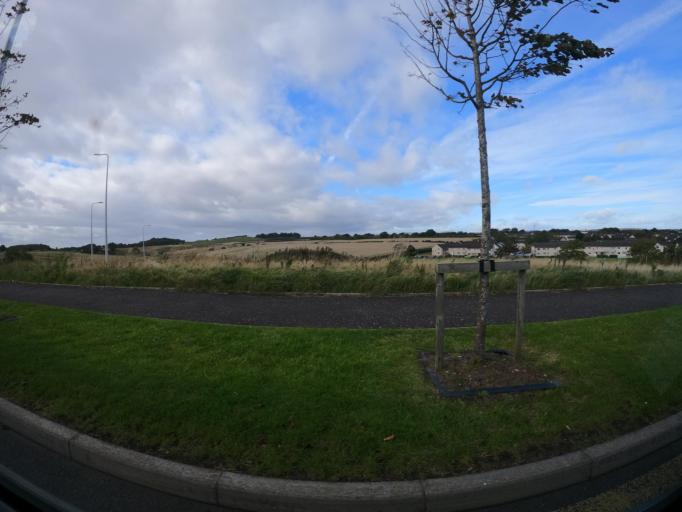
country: GB
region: Scotland
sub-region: Fife
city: Rosyth
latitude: 56.0376
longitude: -3.4380
